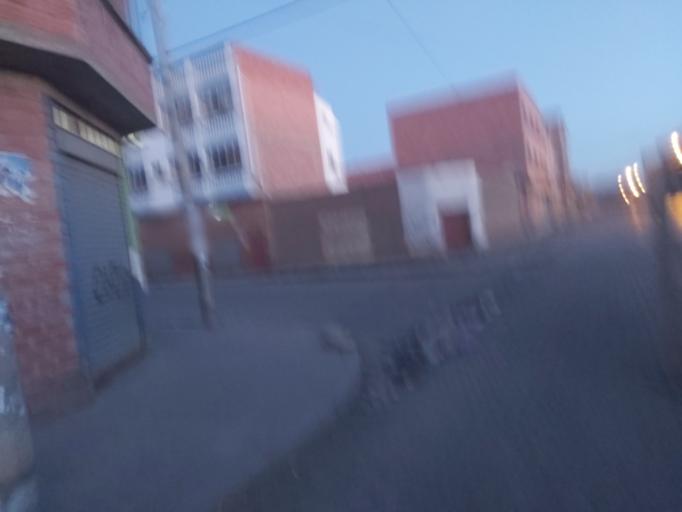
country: BO
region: La Paz
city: La Paz
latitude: -16.5291
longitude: -68.2008
